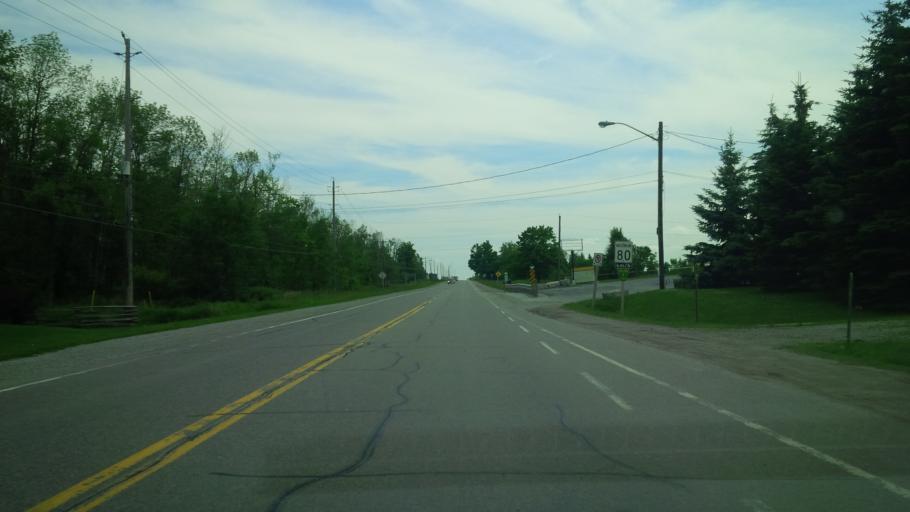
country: CA
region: Ontario
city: Burlington
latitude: 43.4031
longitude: -79.8737
